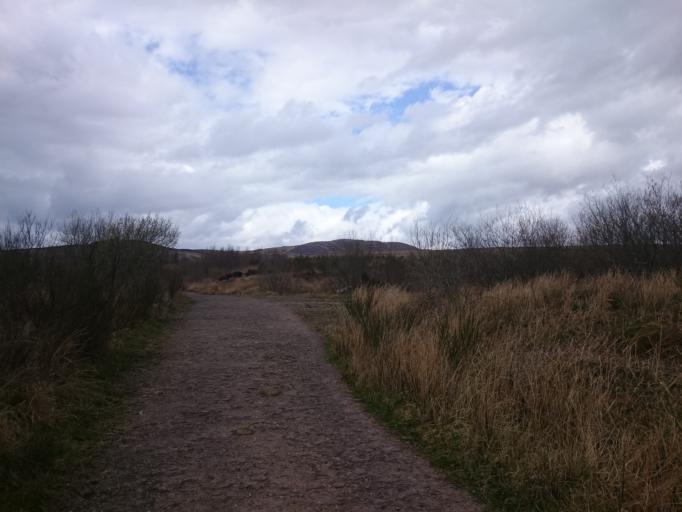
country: GB
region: Scotland
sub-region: Stirling
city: Killearn
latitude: 56.0939
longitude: -4.4883
